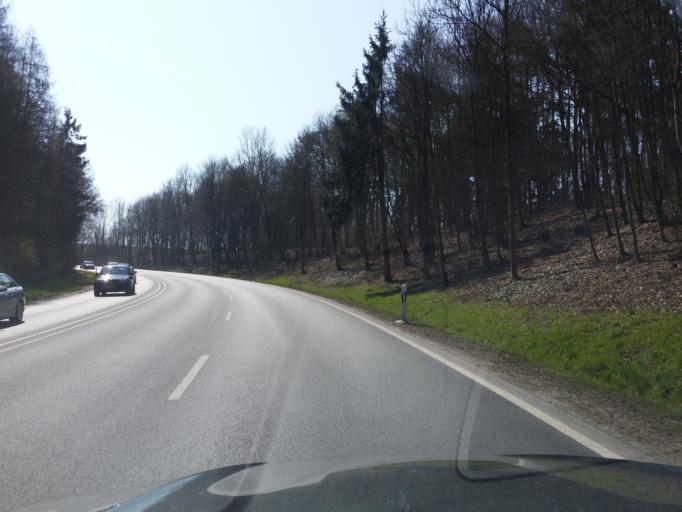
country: DE
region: Bavaria
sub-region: Lower Bavaria
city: Landshut
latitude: 48.5366
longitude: 12.1823
